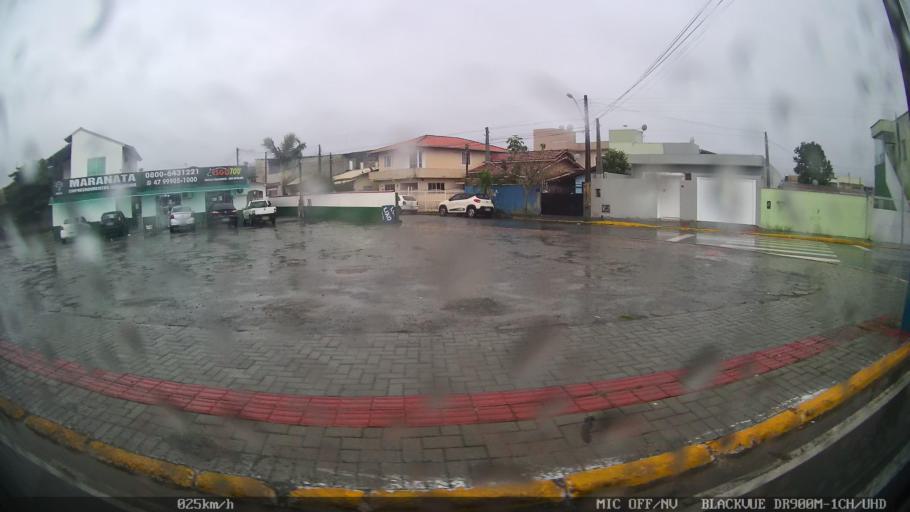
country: BR
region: Santa Catarina
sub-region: Navegantes
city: Navegantes
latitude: -26.8839
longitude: -48.6529
